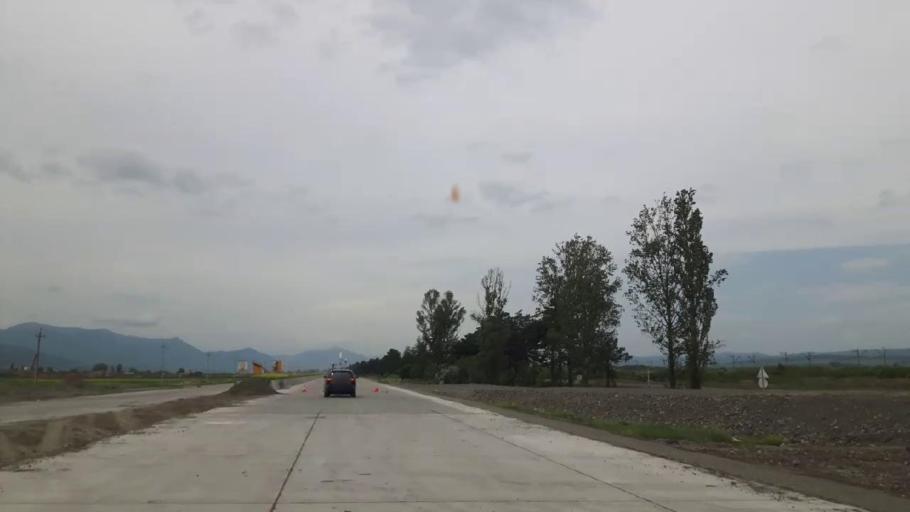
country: GE
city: Agara
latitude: 42.0249
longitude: 43.7600
